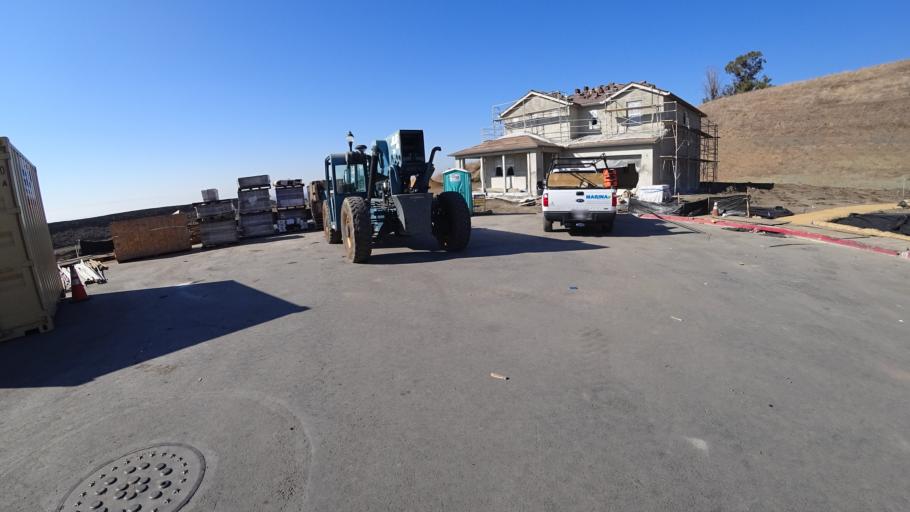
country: US
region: California
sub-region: Alameda County
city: Fairview
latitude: 37.6404
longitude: -122.0492
